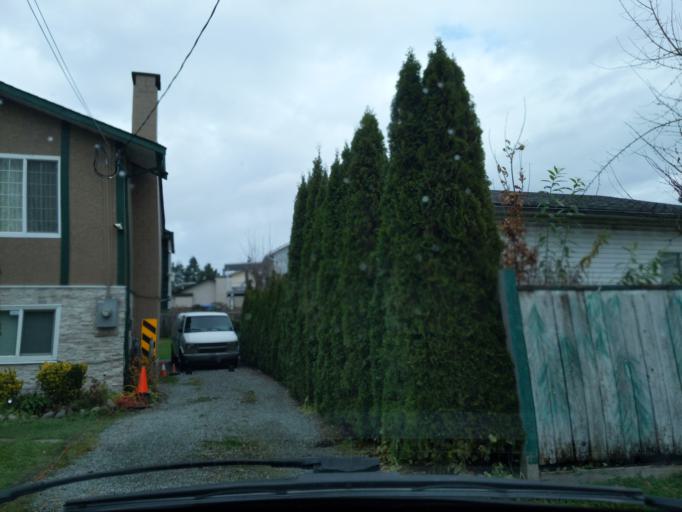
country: CA
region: British Columbia
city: Pitt Meadows
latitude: 49.2114
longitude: -122.6579
